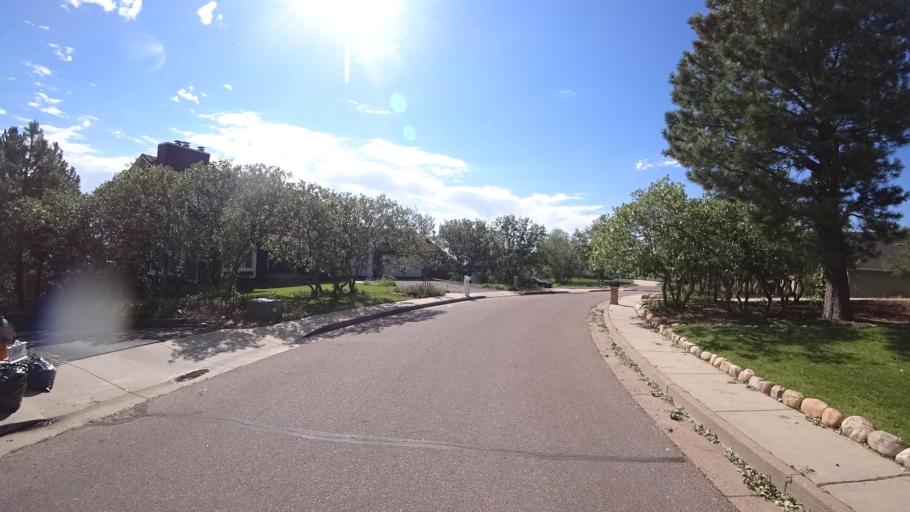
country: US
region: Colorado
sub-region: El Paso County
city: Fort Carson
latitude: 38.7654
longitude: -104.8259
